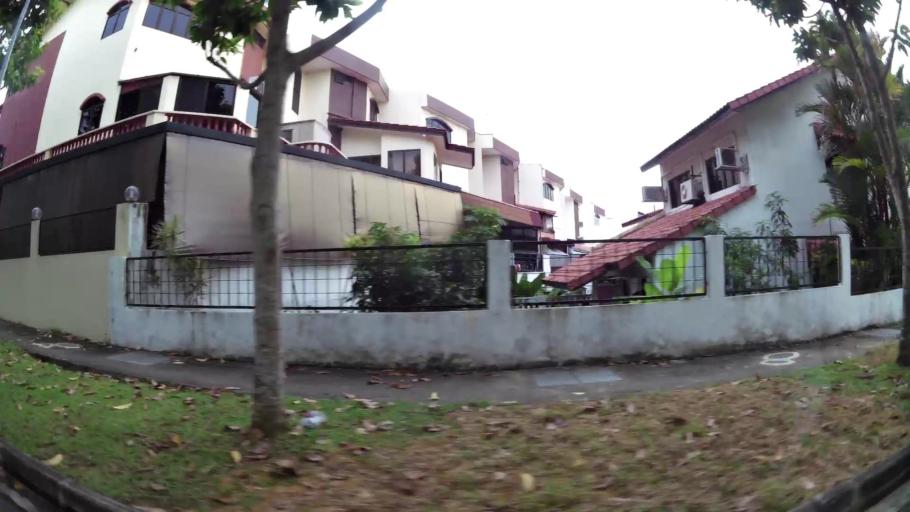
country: SG
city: Singapore
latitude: 1.3479
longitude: 103.8793
